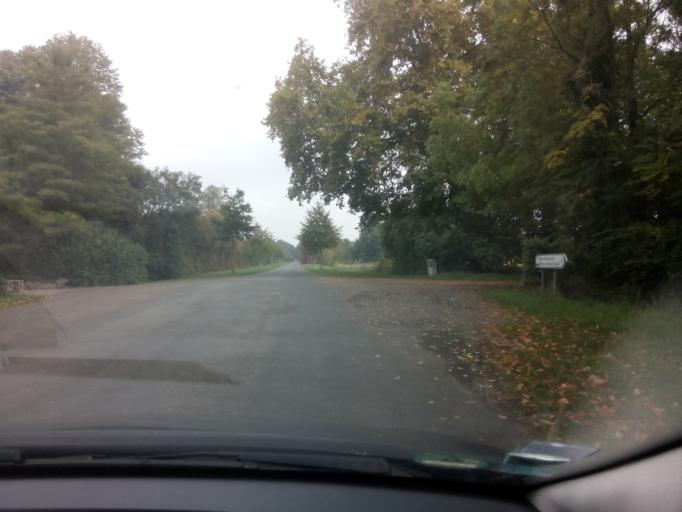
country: FR
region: Pays de la Loire
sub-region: Departement de Maine-et-Loire
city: Soulaire-et-Bourg
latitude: 47.6016
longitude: -0.5424
